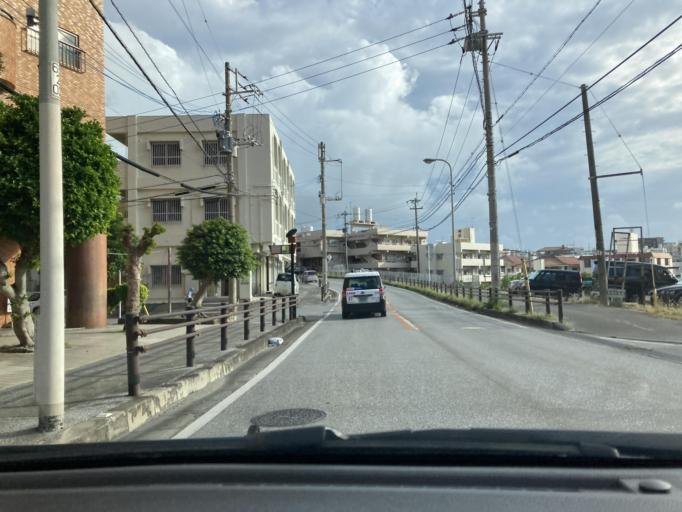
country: JP
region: Okinawa
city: Tomigusuku
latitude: 26.1845
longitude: 127.6608
